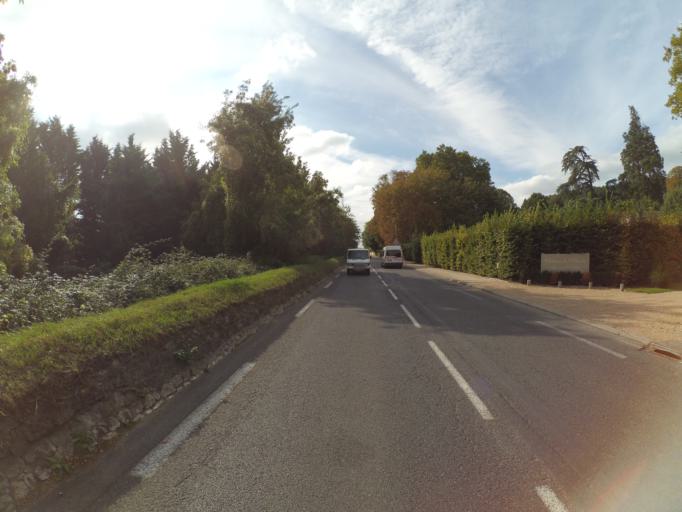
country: FR
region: Centre
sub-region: Departement d'Indre-et-Loire
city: Rochecorbon
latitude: 47.4057
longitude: 0.7362
